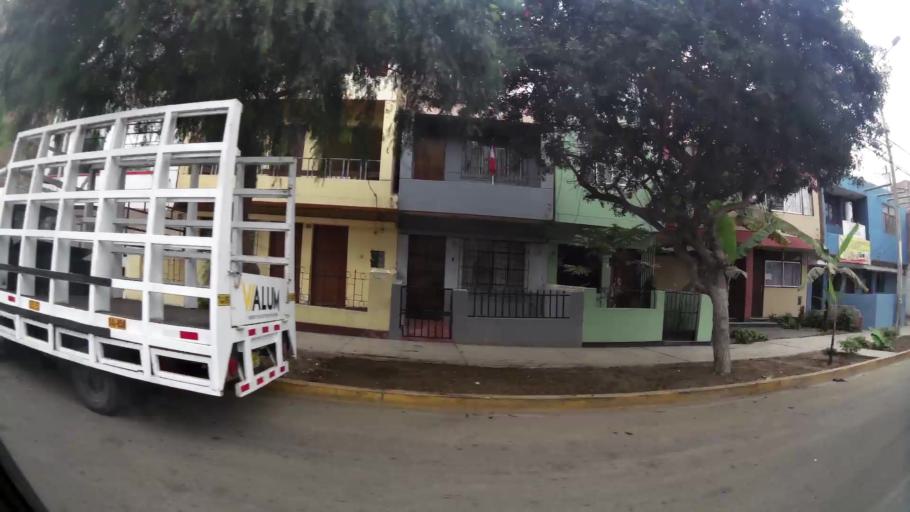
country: PE
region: La Libertad
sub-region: Provincia de Trujillo
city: Trujillo
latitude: -8.1199
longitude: -79.0259
